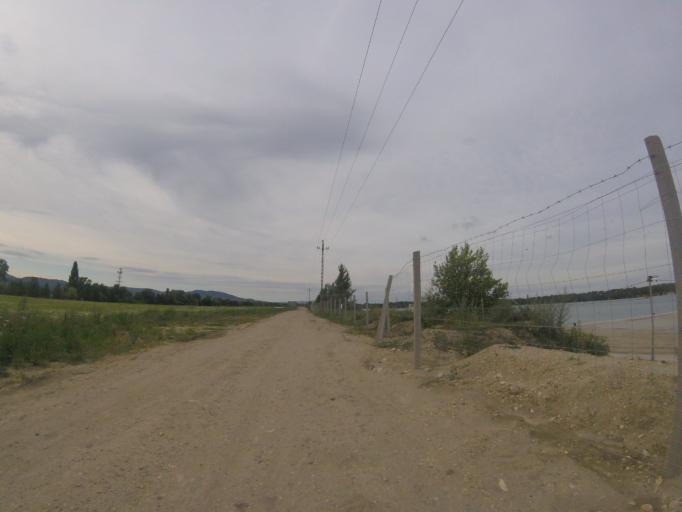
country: HU
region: Pest
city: Budakalasz
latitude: 47.6245
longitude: 19.0697
